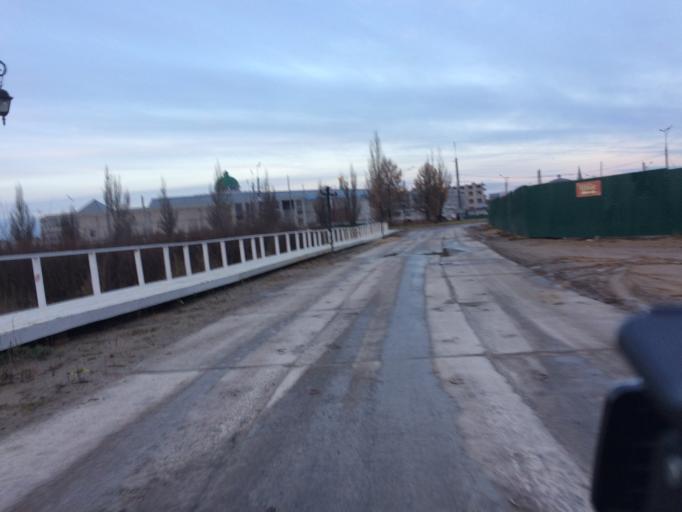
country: RU
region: Mariy-El
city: Yoshkar-Ola
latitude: 56.6267
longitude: 47.9027
